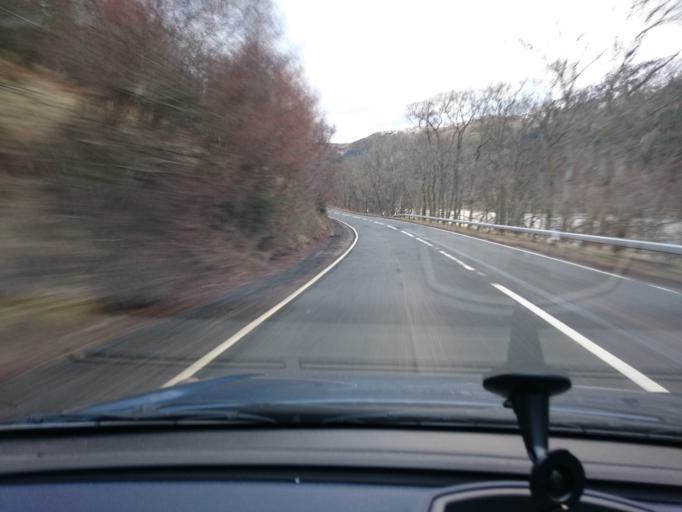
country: GB
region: Scotland
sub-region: Stirling
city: Callander
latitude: 56.2694
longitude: -4.2841
